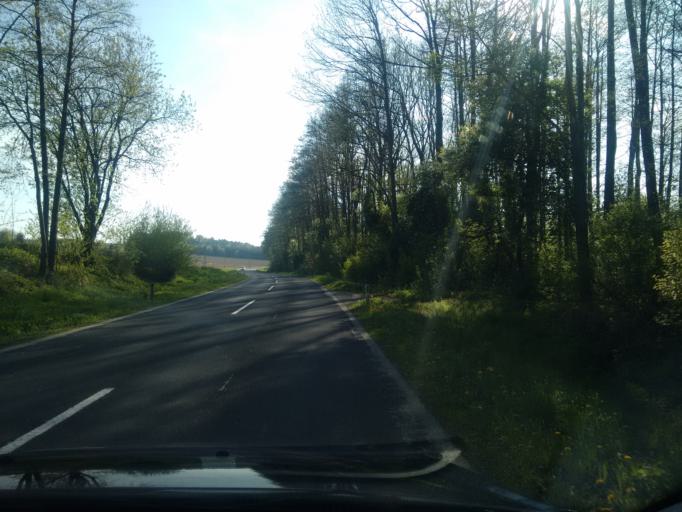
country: AT
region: Upper Austria
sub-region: Wels-Land
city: Buchkirchen
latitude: 48.2198
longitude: 14.0182
